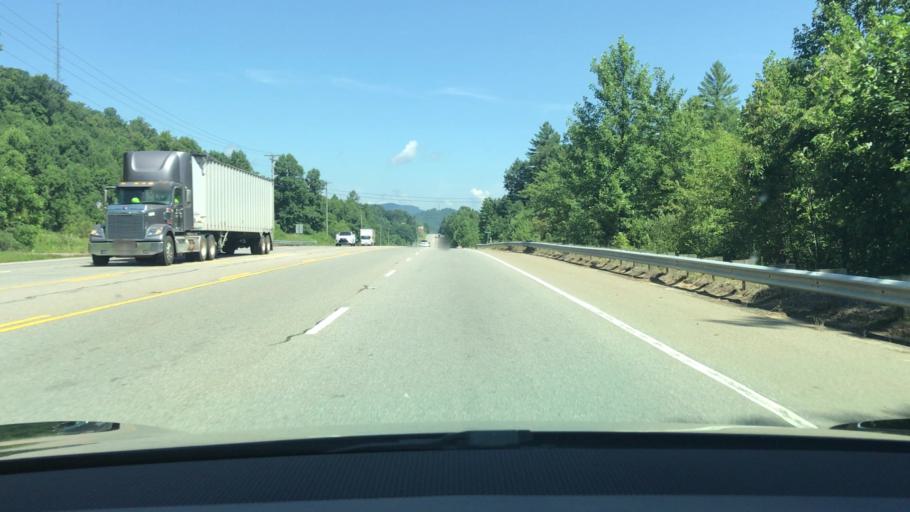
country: US
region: North Carolina
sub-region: Macon County
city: Franklin
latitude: 35.1054
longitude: -83.3865
